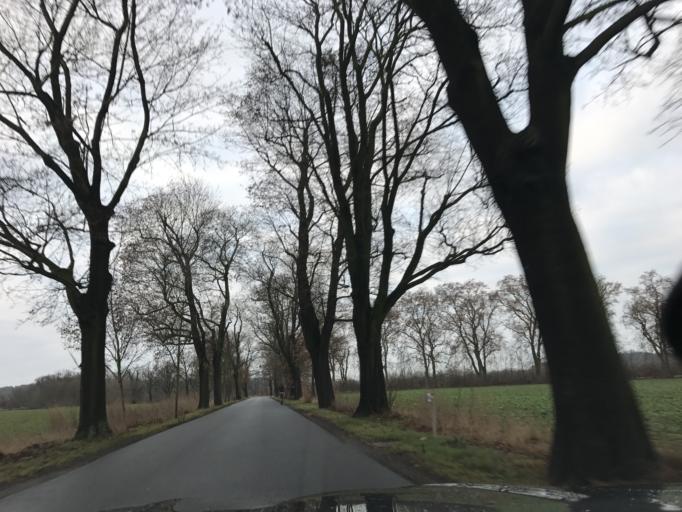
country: DE
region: Brandenburg
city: Potsdam
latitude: 52.4333
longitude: 13.0113
